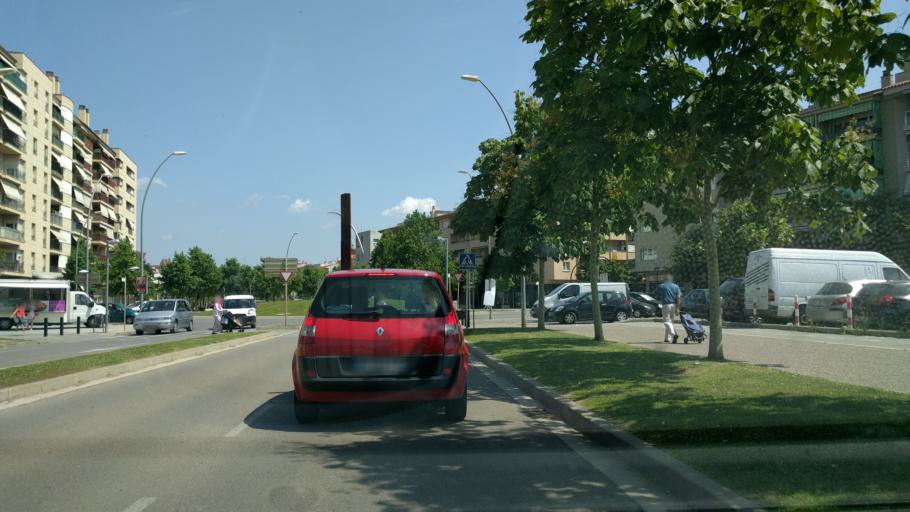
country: ES
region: Catalonia
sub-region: Provincia de Girona
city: Salt
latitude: 41.9737
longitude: 2.8012
